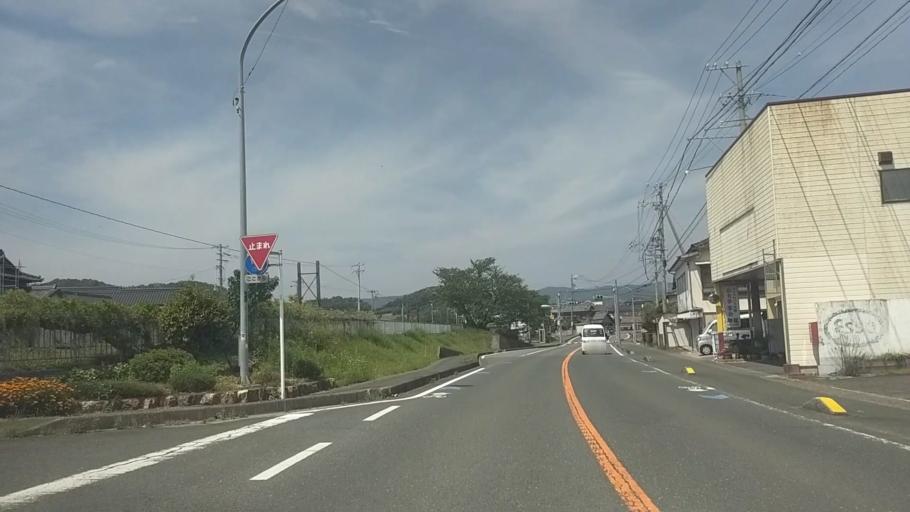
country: JP
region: Shizuoka
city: Kosai-shi
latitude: 34.7827
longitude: 137.5415
